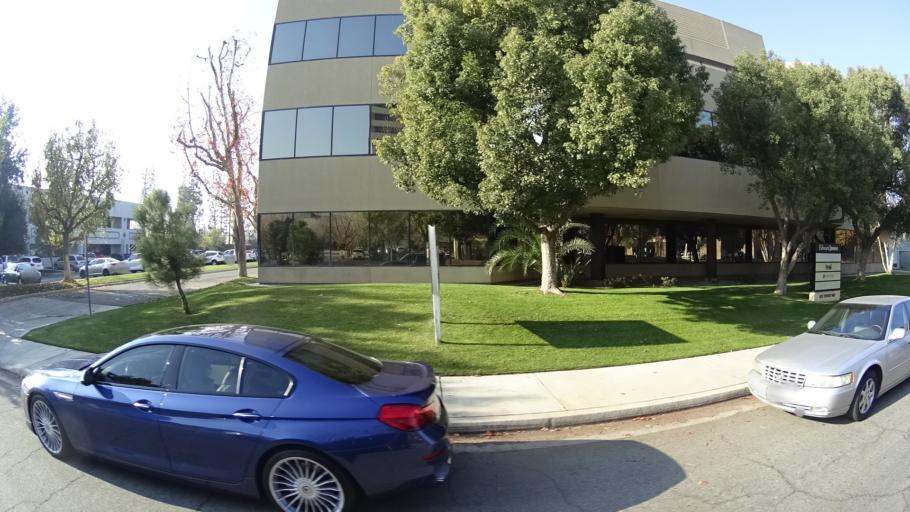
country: US
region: California
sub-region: Kern County
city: Bakersfield
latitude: 35.3631
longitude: -119.0617
